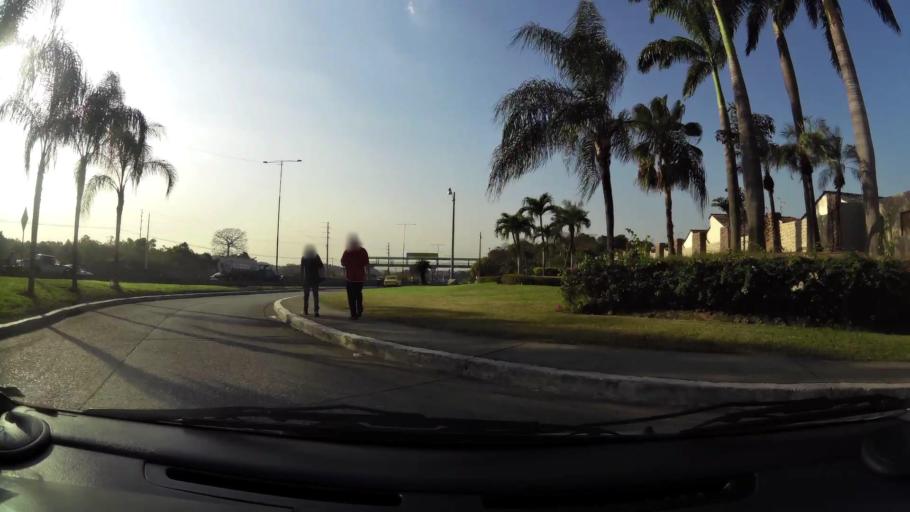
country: EC
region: Guayas
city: Santa Lucia
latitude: -2.1507
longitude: -79.9459
